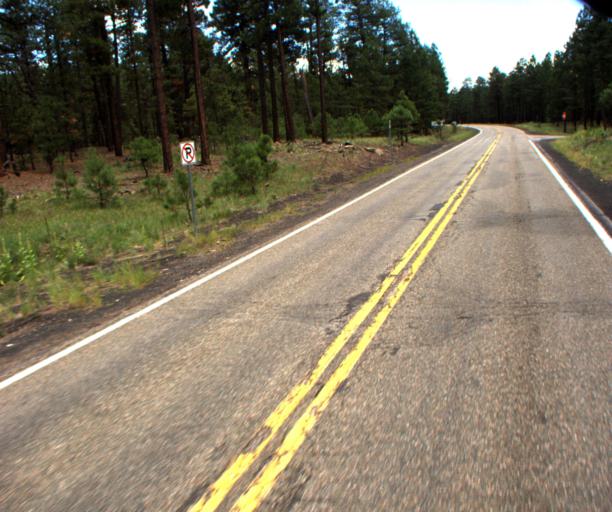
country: US
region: Arizona
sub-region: Coconino County
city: Flagstaff
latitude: 35.2872
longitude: -111.7603
